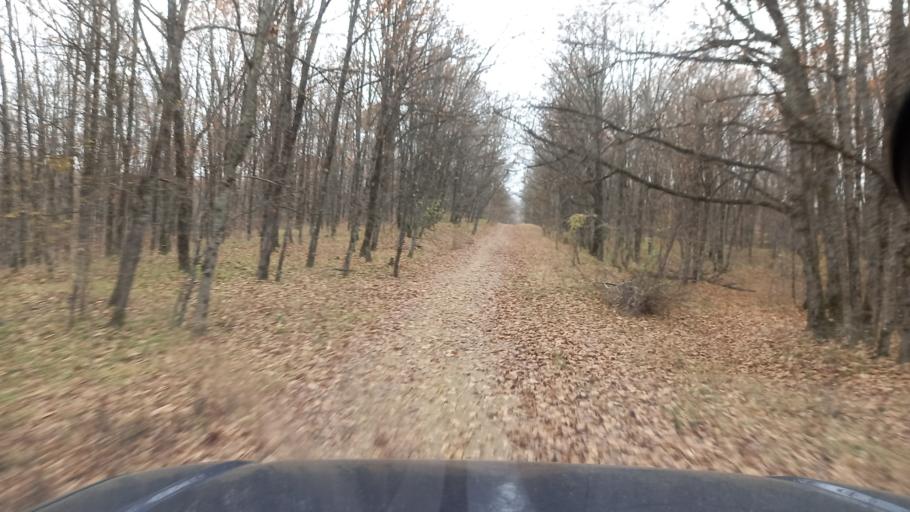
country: RU
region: Krasnodarskiy
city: Goryachiy Klyuch
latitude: 44.5003
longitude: 39.2822
